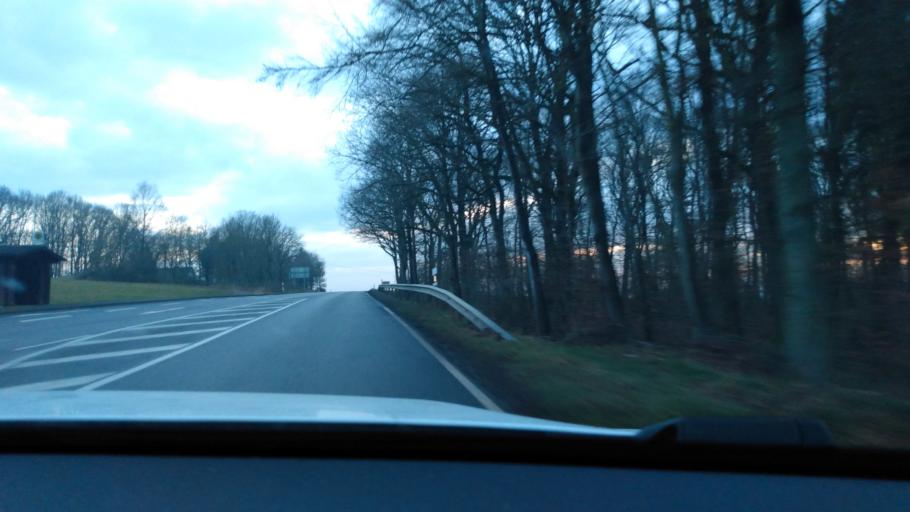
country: DE
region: Rheinland-Pfalz
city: Kircheib
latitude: 50.7072
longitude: 7.4372
